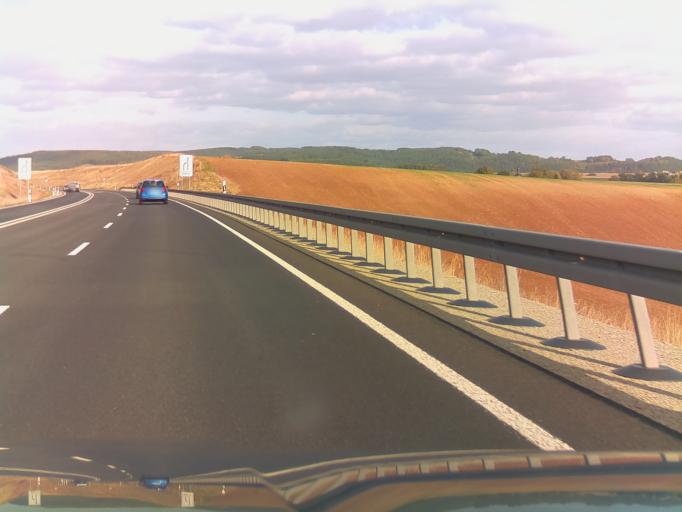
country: DE
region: Thuringia
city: Behringen
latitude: 50.7527
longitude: 11.0267
